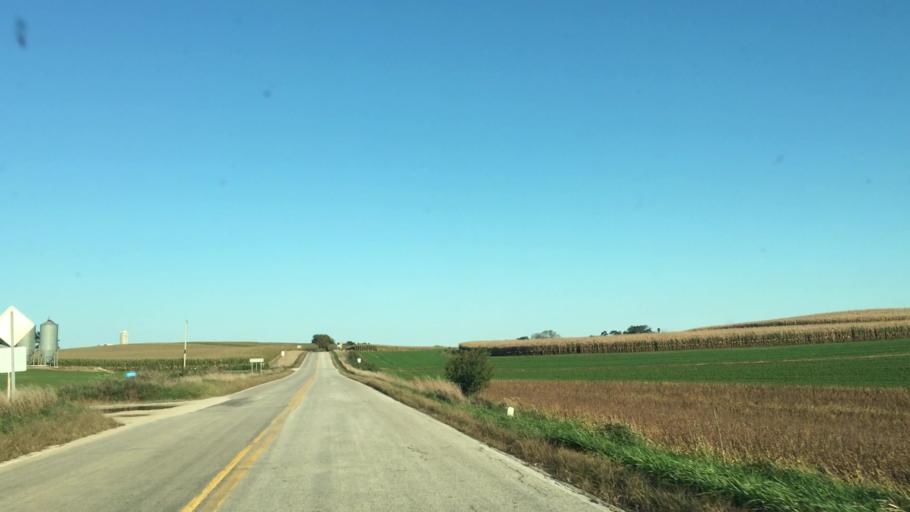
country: US
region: Minnesota
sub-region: Fillmore County
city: Chatfield
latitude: 43.8184
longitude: -92.0668
